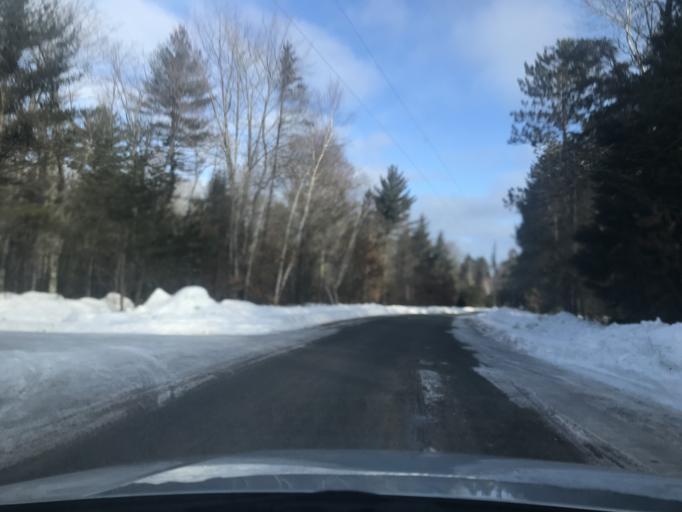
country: US
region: Wisconsin
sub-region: Marinette County
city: Niagara
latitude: 45.6315
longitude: -87.9680
